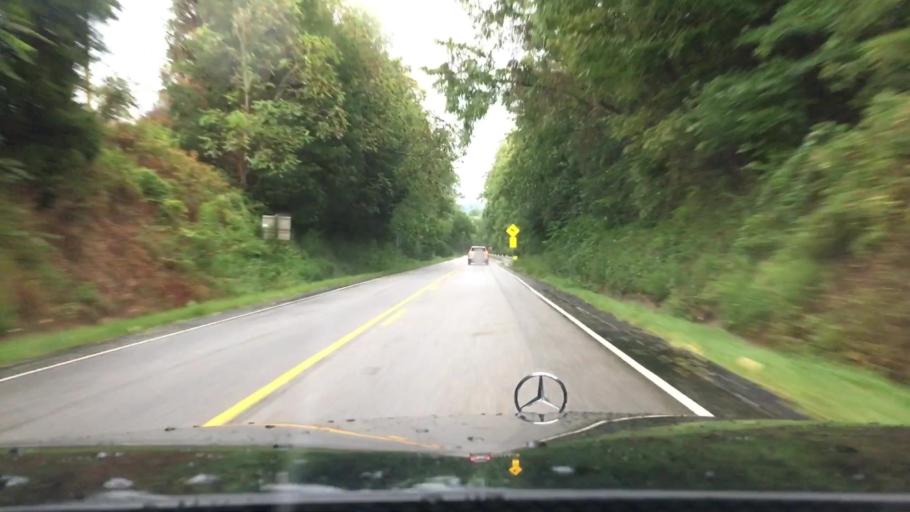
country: US
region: Virginia
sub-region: Amherst County
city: Amherst
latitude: 37.6785
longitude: -79.0201
